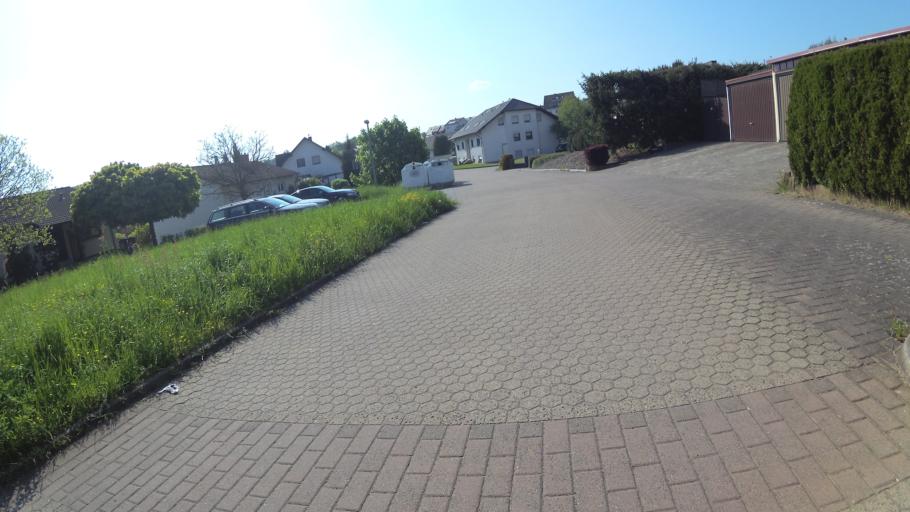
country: DE
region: Saarland
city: Illingen
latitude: 49.3638
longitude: 7.0458
